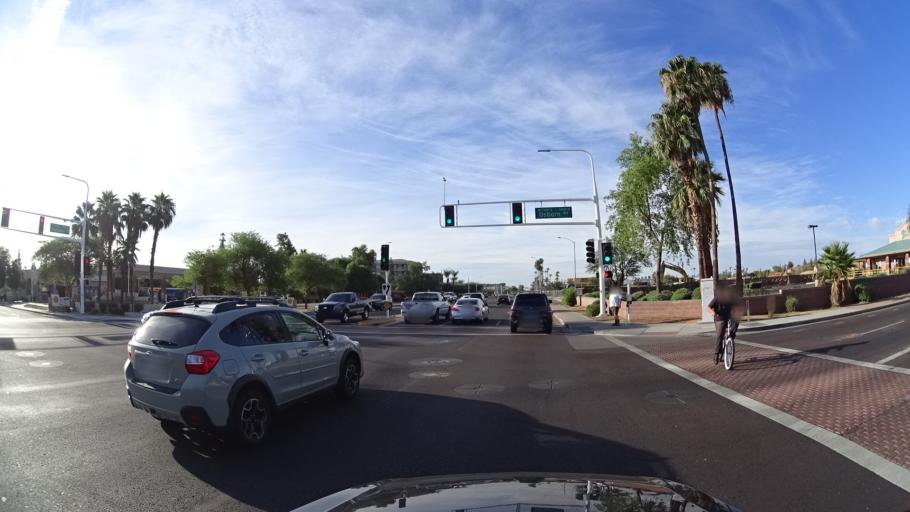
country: US
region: Arizona
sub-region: Maricopa County
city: Scottsdale
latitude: 33.4877
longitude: -111.9263
